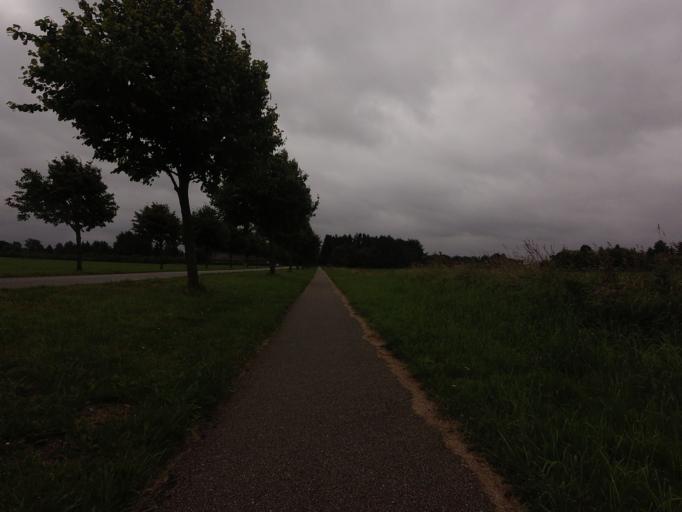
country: DK
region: Central Jutland
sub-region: Horsens Kommune
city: Braedstrup
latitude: 55.9827
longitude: 9.5950
